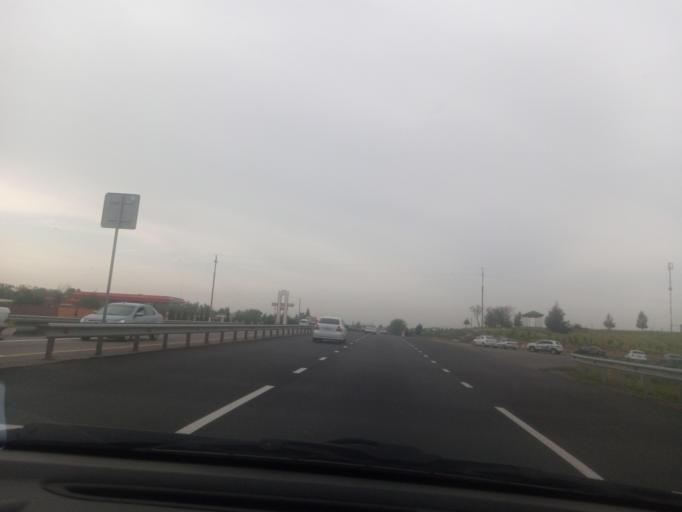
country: UZ
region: Toshkent
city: Tuytepa
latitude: 41.1237
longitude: 69.4395
